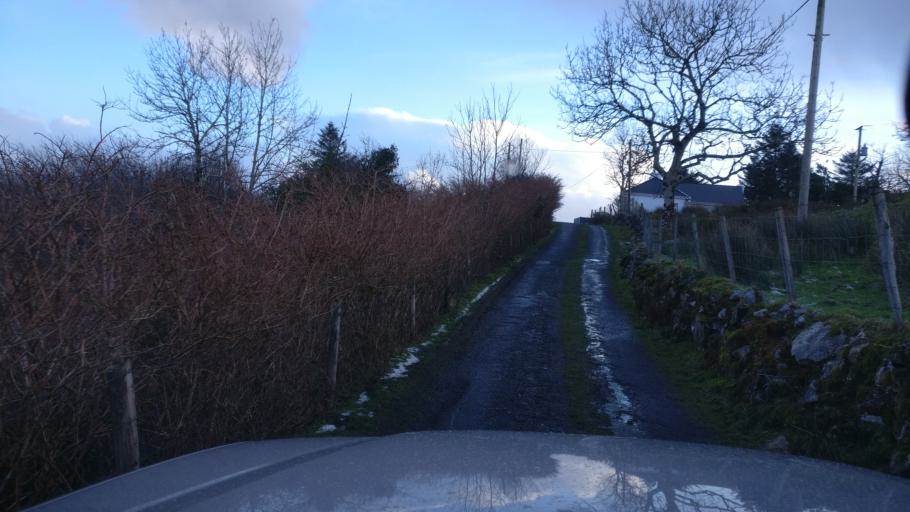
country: IE
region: Connaught
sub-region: County Galway
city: Clifden
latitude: 53.4870
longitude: -9.6980
